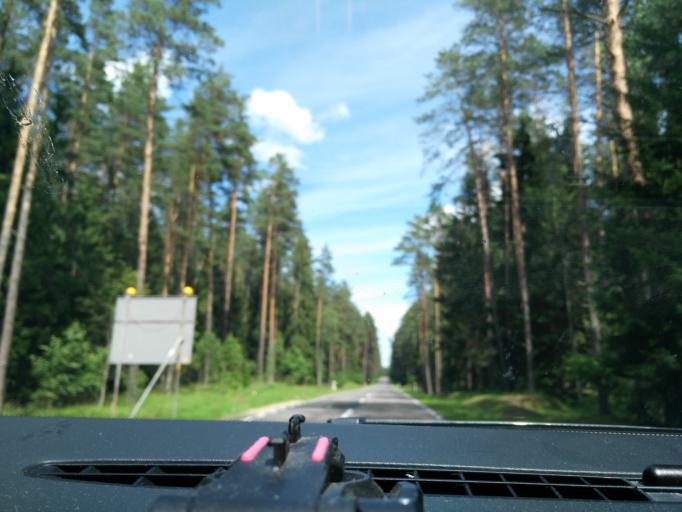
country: PL
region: Podlasie
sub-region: Powiat sejnenski
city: Krasnopol
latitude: 53.9671
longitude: 23.2449
